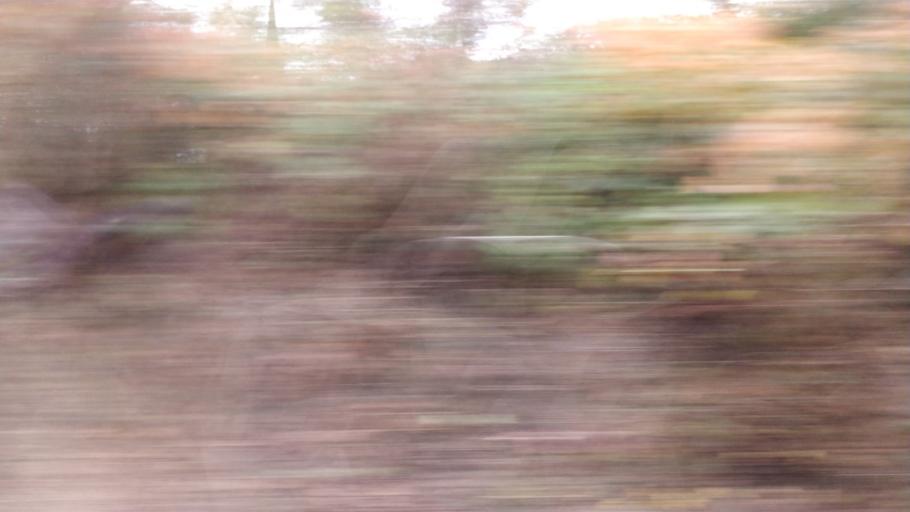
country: GB
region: England
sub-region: Lancashire
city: Parbold
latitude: 53.5896
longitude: -2.7649
